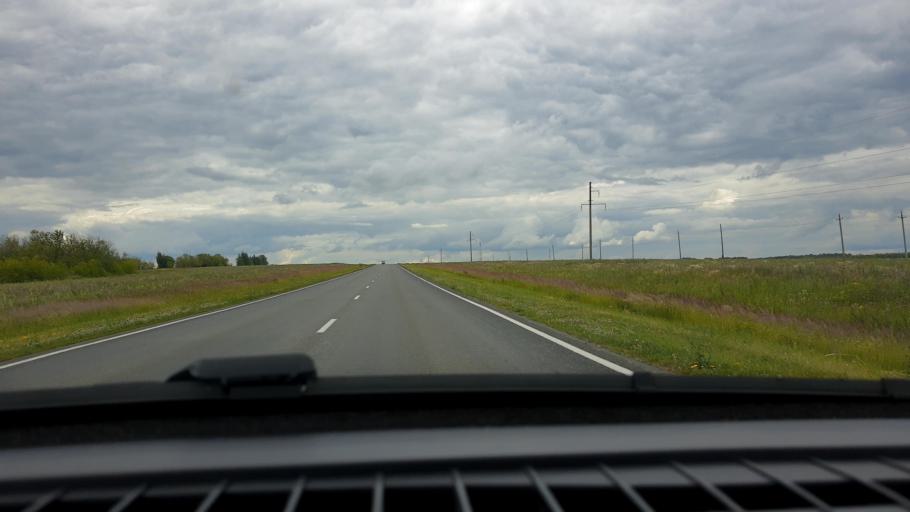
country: RU
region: Nizjnij Novgorod
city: Sergach
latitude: 55.5446
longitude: 45.5108
